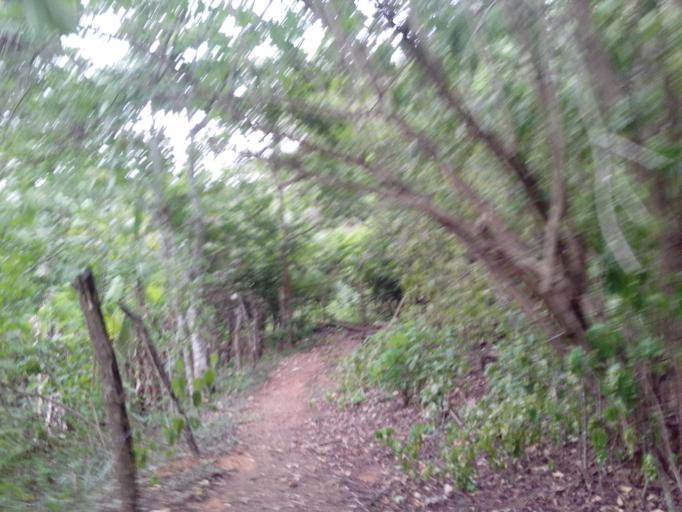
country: BR
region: Rio de Janeiro
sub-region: Miguel Pereira
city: Miguel Pereira
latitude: -22.5090
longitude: -43.5182
